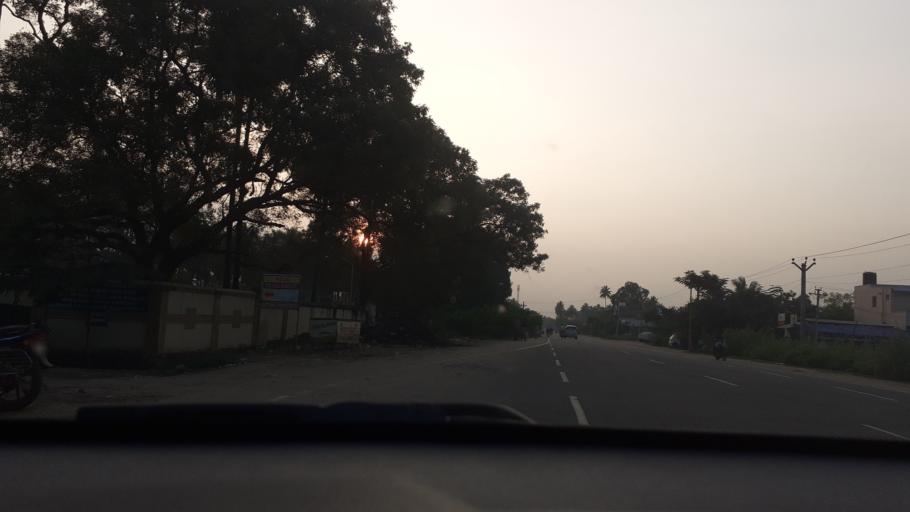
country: IN
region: Tamil Nadu
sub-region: Dindigul
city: Palani
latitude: 10.4327
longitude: 77.5229
